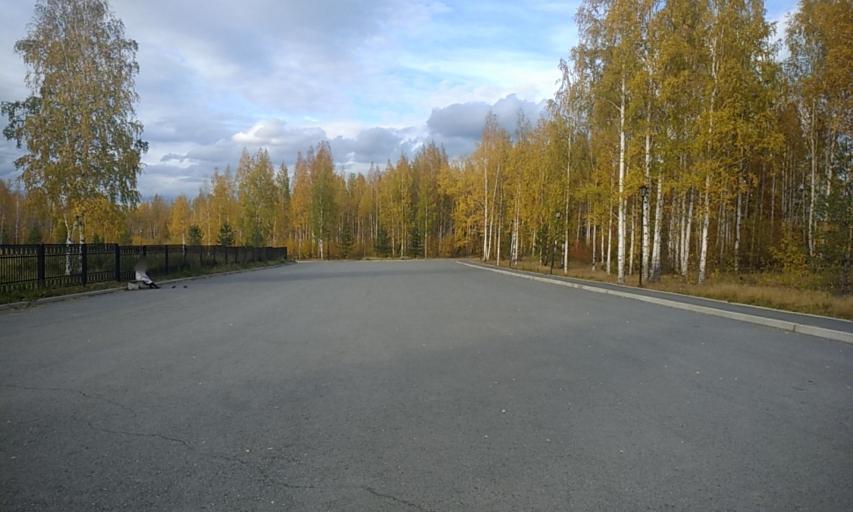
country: RU
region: Sverdlovsk
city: Krasnoural'sk
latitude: 58.3546
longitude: 60.0532
